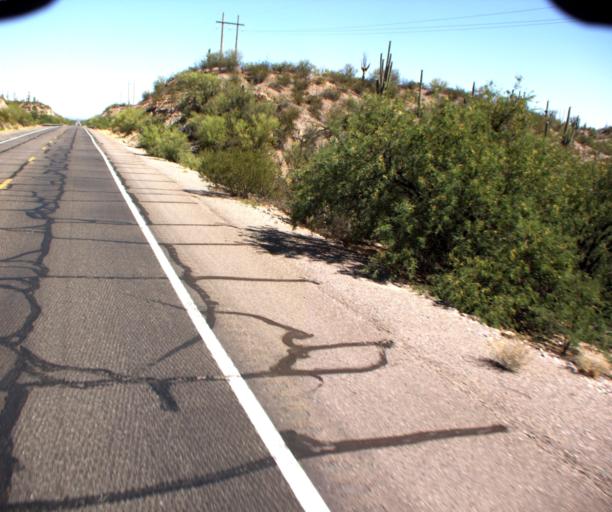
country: US
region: Arizona
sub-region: Pinal County
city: Mammoth
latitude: 32.7597
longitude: -110.6515
